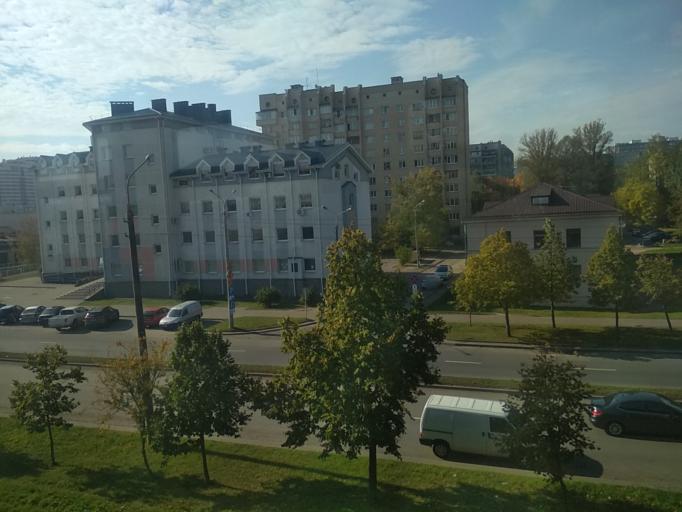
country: BY
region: Minsk
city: Minsk
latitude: 53.8752
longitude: 27.5624
